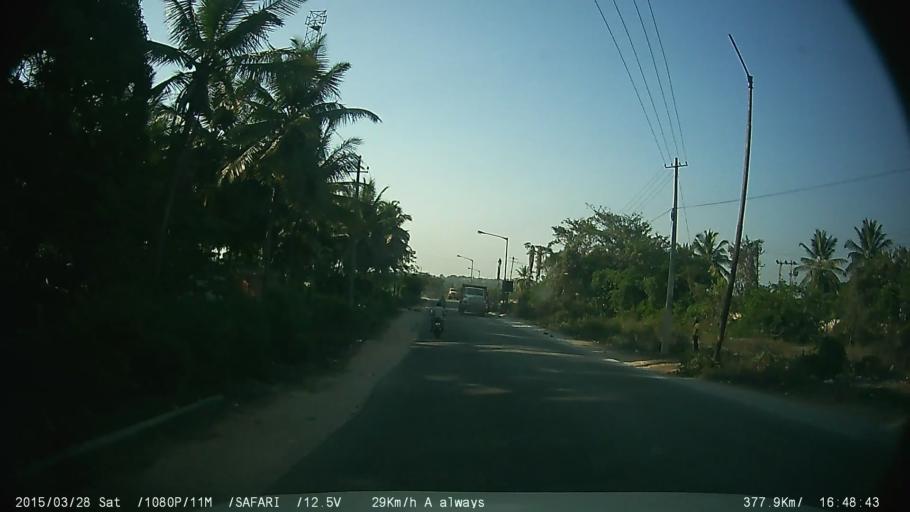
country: IN
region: Karnataka
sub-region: Mandya
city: Shrirangapattana
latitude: 12.4172
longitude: 76.5811
